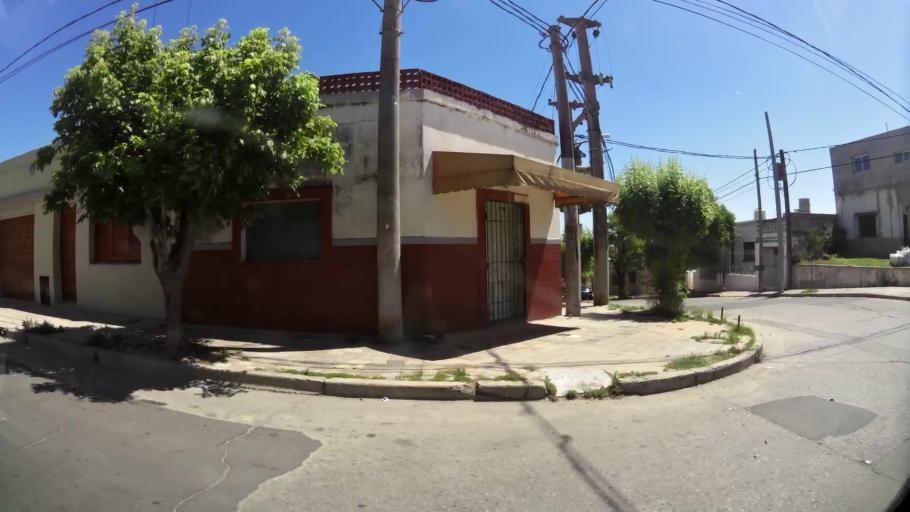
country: AR
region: Cordoba
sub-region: Departamento de Capital
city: Cordoba
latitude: -31.4276
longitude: -64.1499
